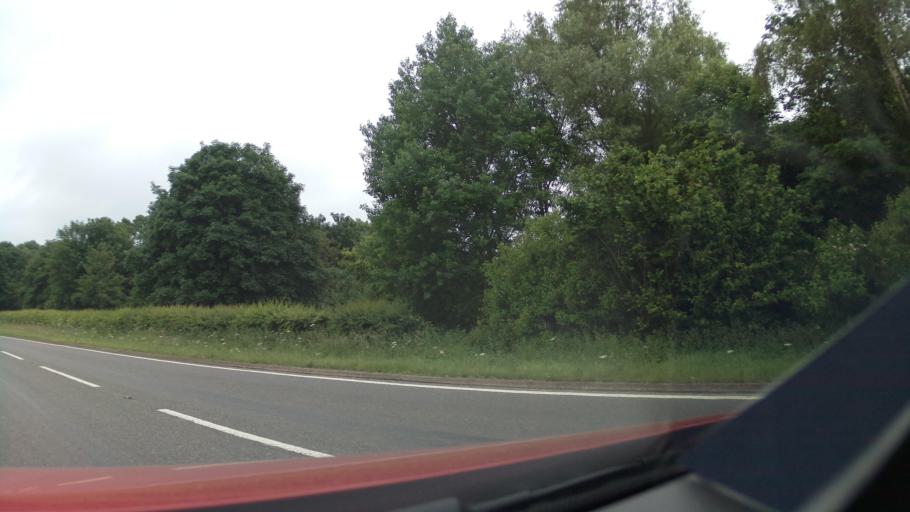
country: GB
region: England
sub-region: District of Rutland
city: Ridlington
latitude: 52.5998
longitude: -0.8710
